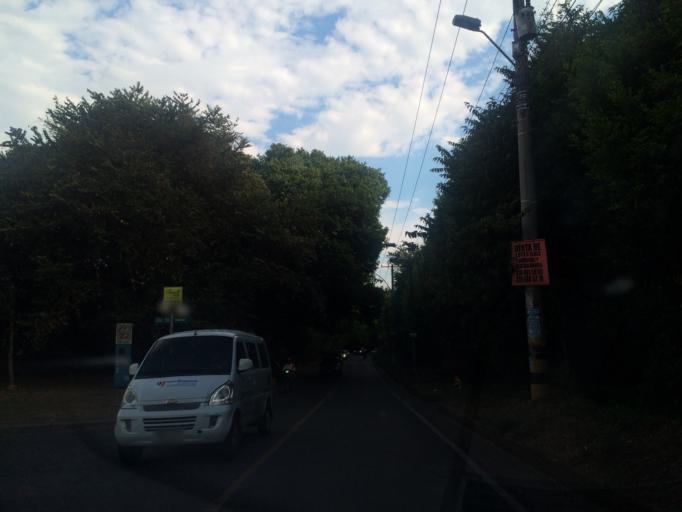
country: CO
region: Valle del Cauca
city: Cali
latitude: 3.3689
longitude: -76.5417
